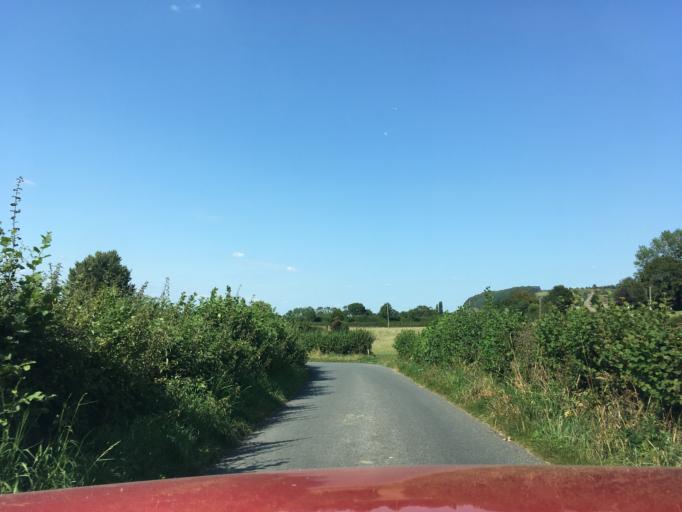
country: GB
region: England
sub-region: Gloucestershire
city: Dursley
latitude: 51.6959
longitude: -2.3161
